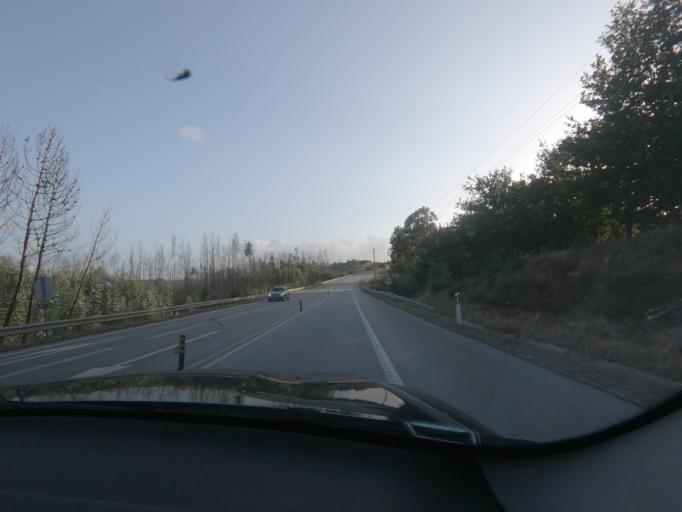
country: PT
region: Viseu
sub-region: Santa Comba Dao
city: Santa Comba Dao
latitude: 40.3519
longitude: -8.1570
